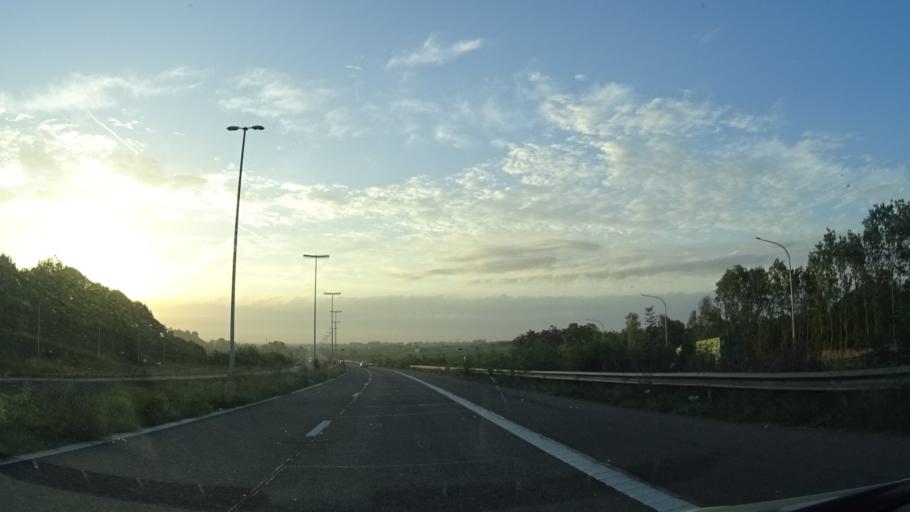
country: BE
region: Wallonia
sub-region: Province du Hainaut
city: Frameries
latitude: 50.4153
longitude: 3.9237
